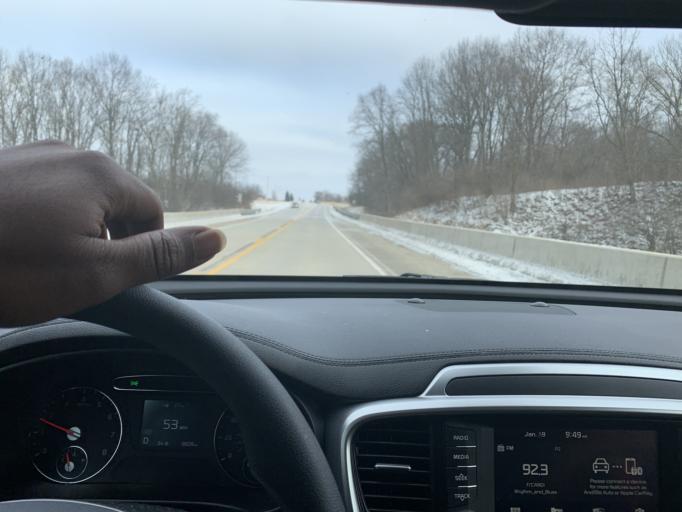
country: US
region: Illinois
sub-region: Will County
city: Fairmont
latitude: 41.5482
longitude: -88.0438
